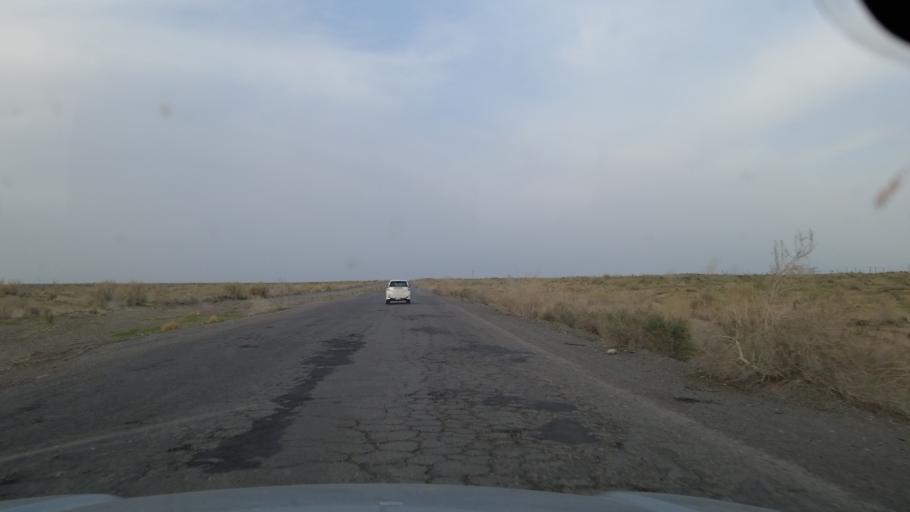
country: TM
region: Mary
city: Bayramaly
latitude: 38.2705
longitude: 62.9482
